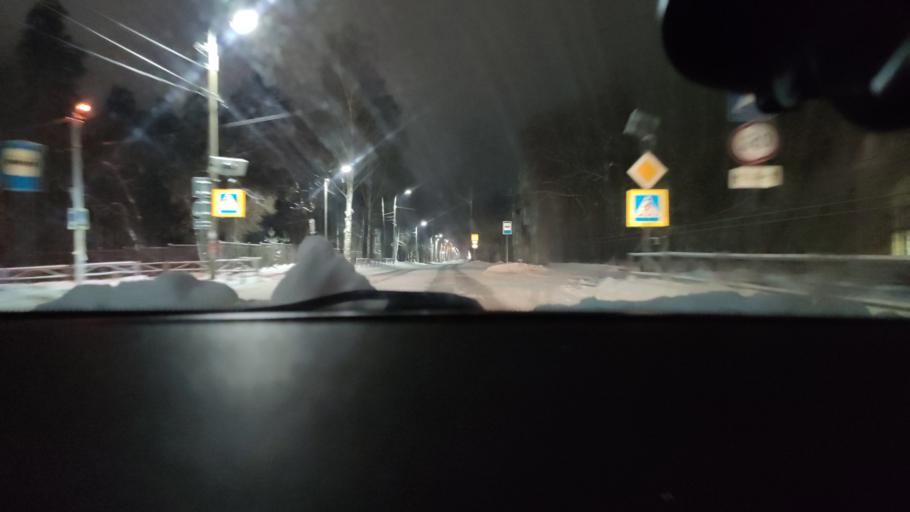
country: RU
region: Perm
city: Krasnokamsk
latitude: 58.0843
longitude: 55.7454
